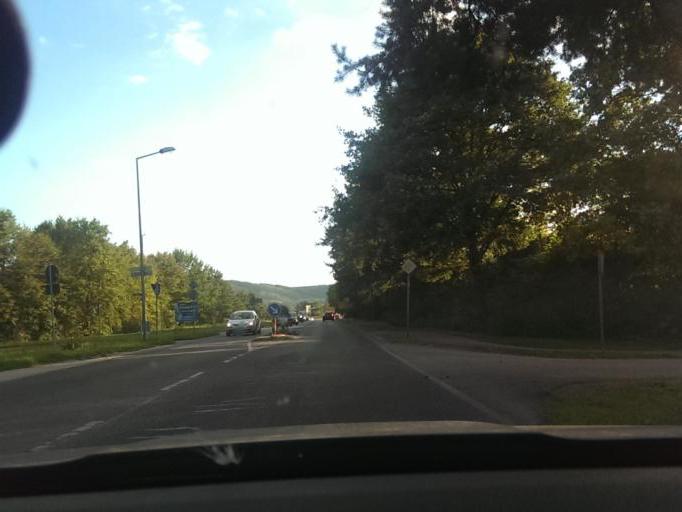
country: DE
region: Baden-Wuerttemberg
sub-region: Karlsruhe Region
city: Karlsruhe
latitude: 48.9894
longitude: 8.4482
